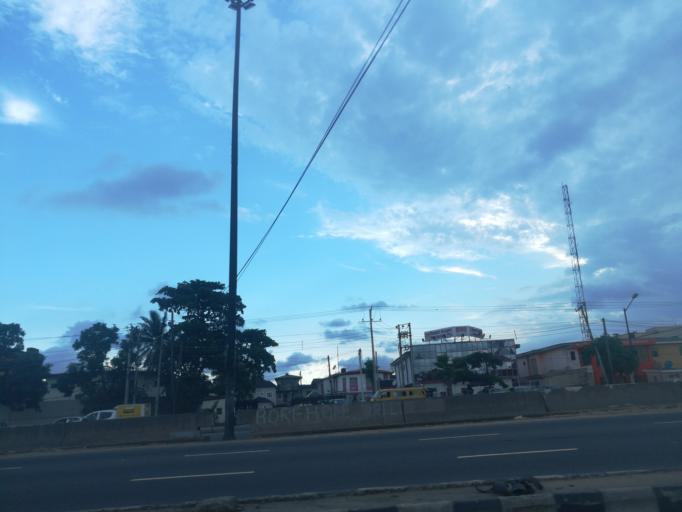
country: NG
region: Lagos
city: Somolu
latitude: 6.5501
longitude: 3.3775
